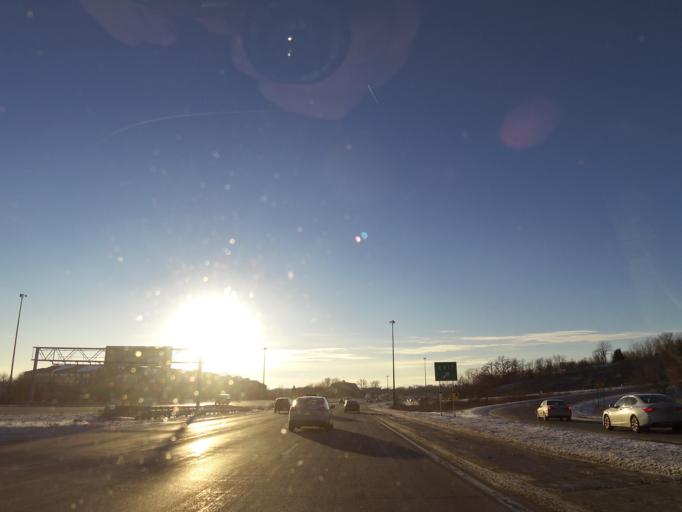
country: US
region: Minnesota
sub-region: Hennepin County
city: Eden Prairie
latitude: 44.8622
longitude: -93.4438
